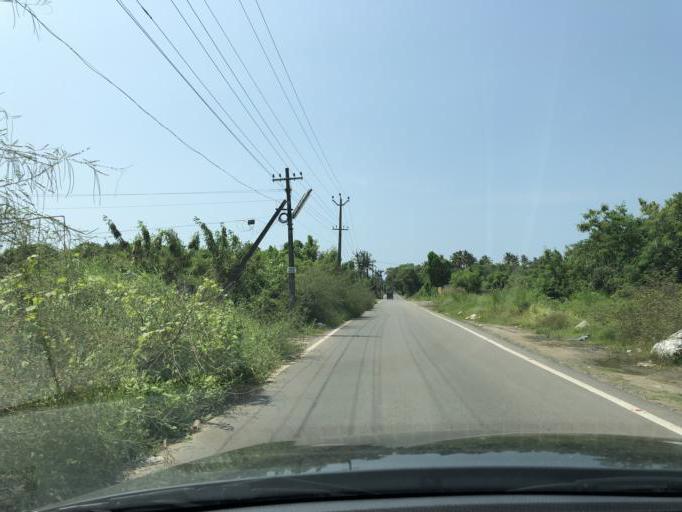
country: IN
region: Kerala
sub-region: Ernakulam
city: Cochin
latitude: 9.9908
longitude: 76.2335
